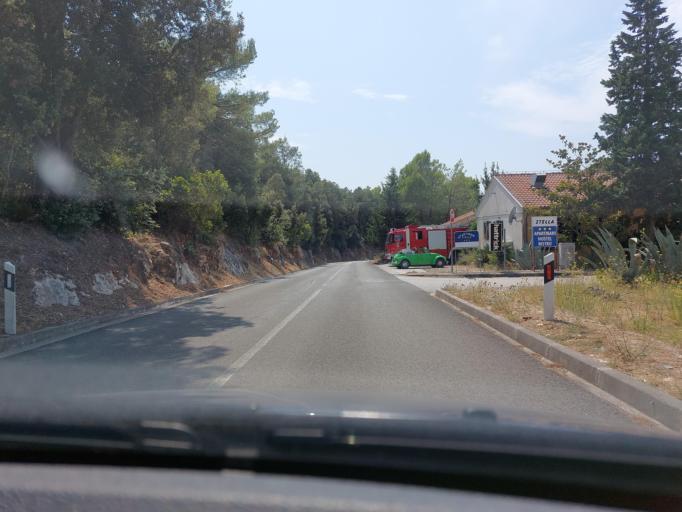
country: HR
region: Dubrovacko-Neretvanska
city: Smokvica
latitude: 42.7454
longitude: 16.8330
